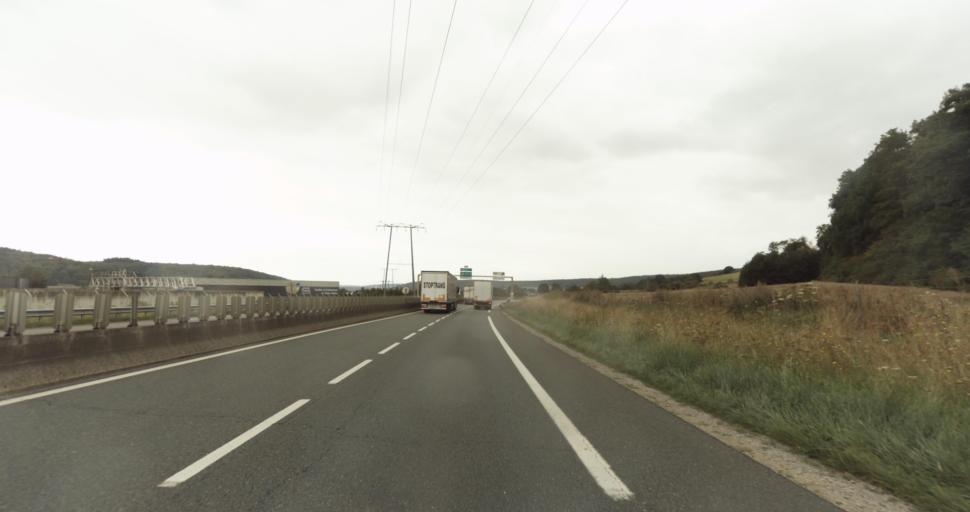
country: FR
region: Haute-Normandie
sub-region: Departement de l'Eure
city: Gravigny
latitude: 49.0554
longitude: 1.1758
